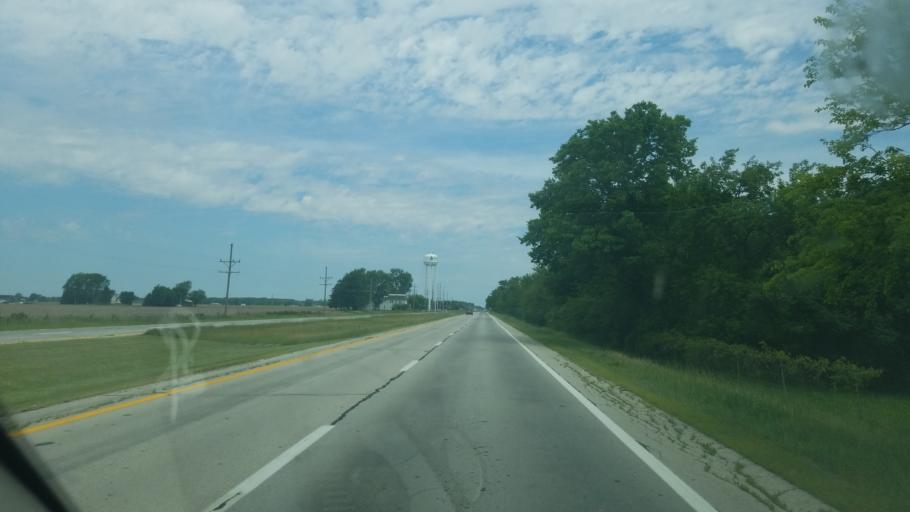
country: US
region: Ohio
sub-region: Wood County
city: North Baltimore
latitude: 41.2638
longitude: -83.6500
